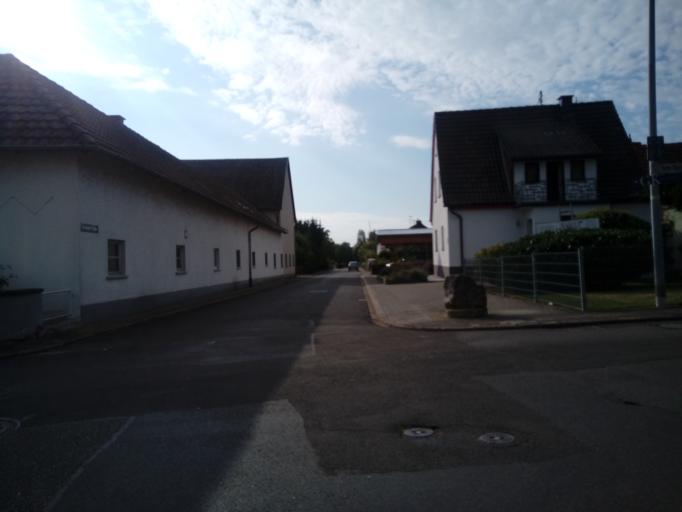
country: DE
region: Rheinland-Pfalz
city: Gutenberg
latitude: 49.8785
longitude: 7.7992
